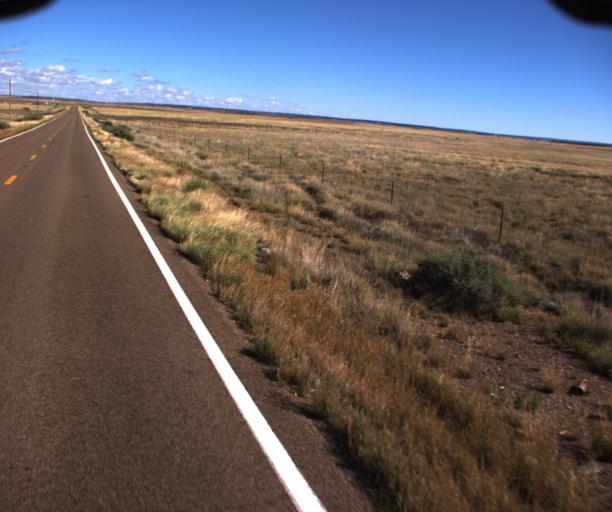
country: US
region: Arizona
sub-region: Apache County
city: Saint Johns
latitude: 34.5915
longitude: -109.3285
